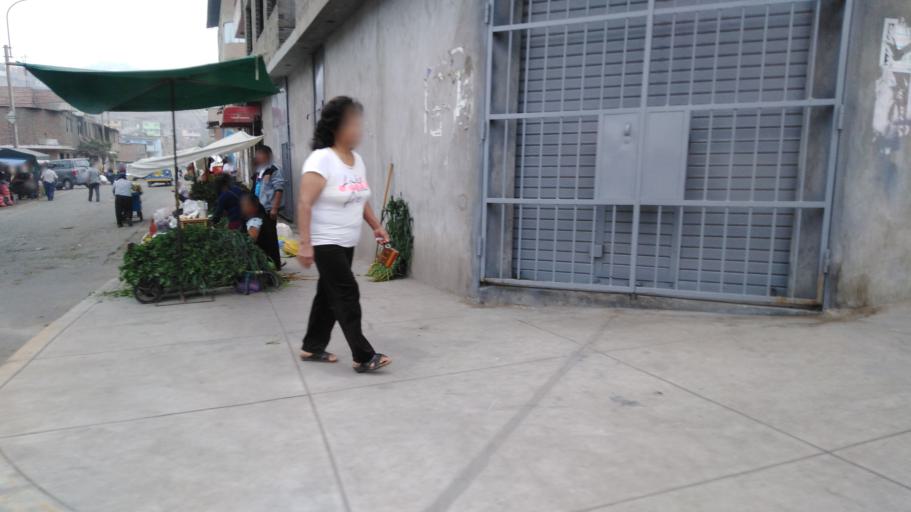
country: PE
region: Lima
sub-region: Lima
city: La Molina
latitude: -12.1430
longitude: -76.9436
